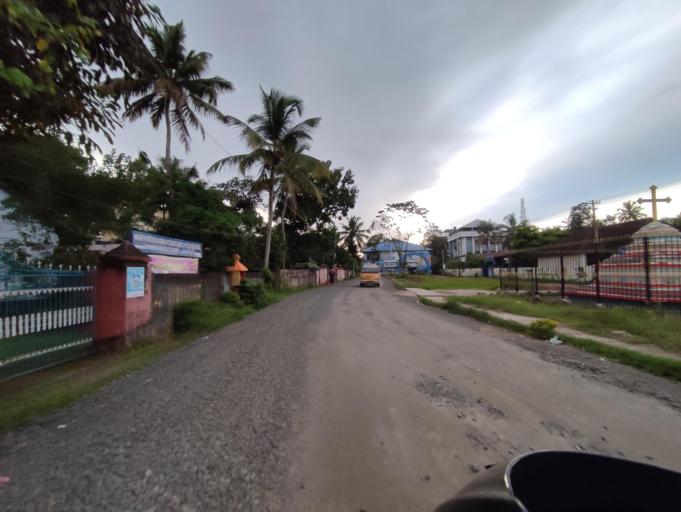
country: IN
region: Kerala
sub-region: Alappuzha
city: Vayalar
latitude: 9.6889
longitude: 76.3347
